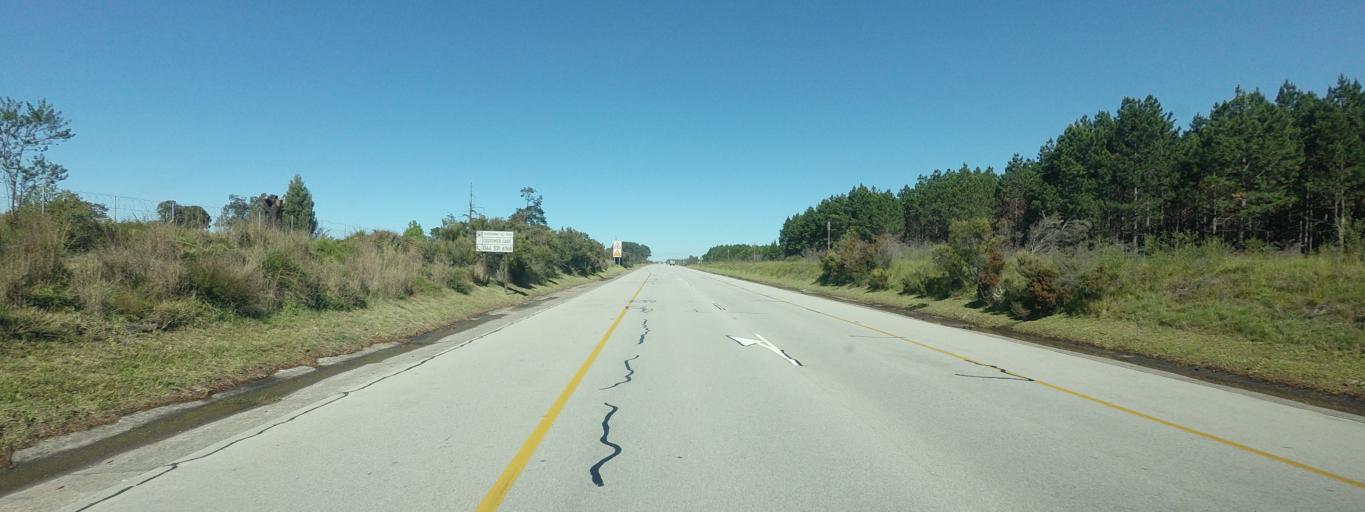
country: ZA
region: Western Cape
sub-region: Eden District Municipality
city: Plettenberg Bay
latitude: -33.9727
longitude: 23.8249
